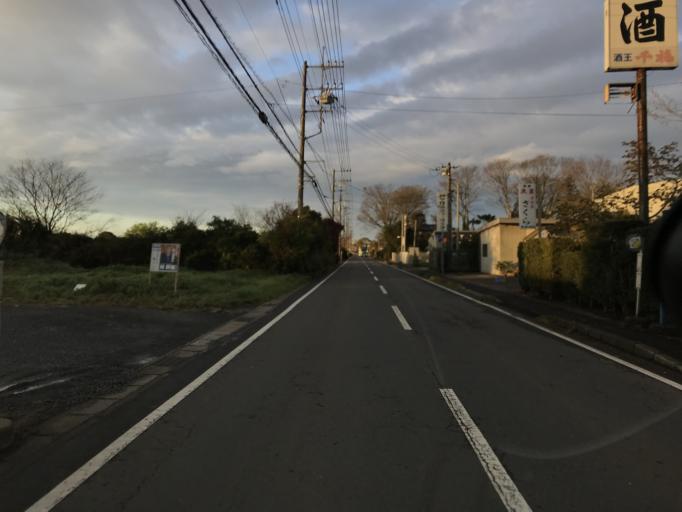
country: JP
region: Chiba
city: Sawara
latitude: 35.8215
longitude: 140.4564
